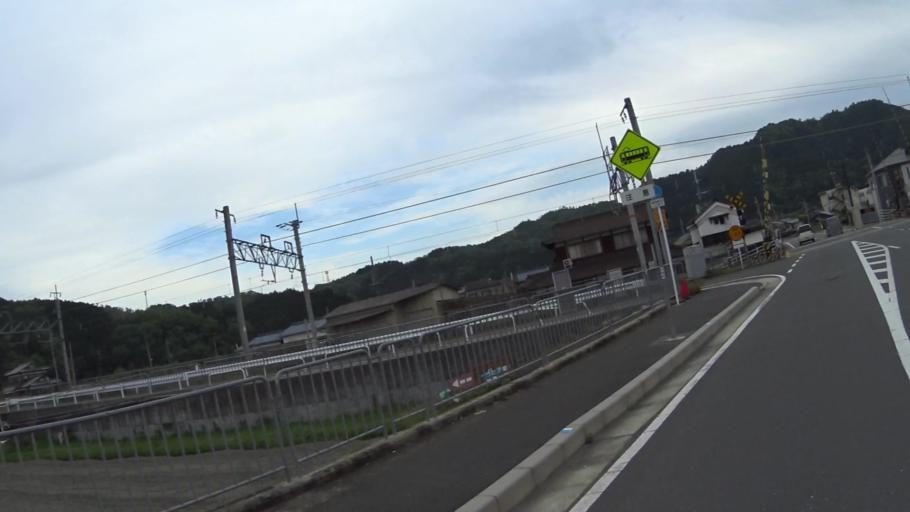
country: JP
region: Kyoto
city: Kameoka
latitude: 35.0685
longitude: 135.5342
